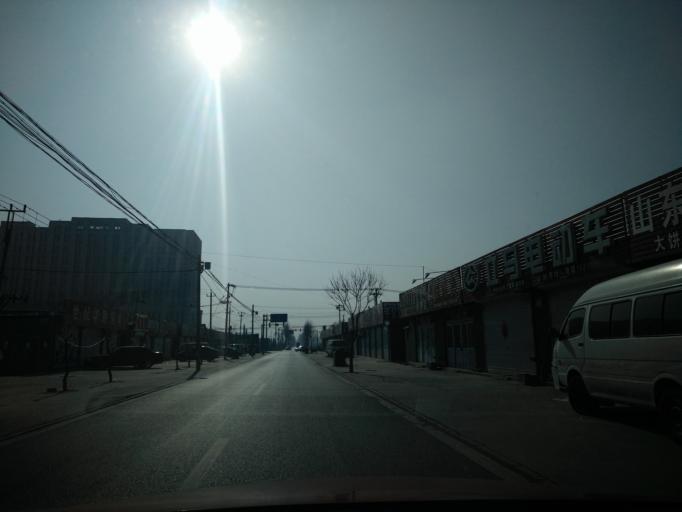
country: CN
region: Beijing
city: Yinghai
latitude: 39.7086
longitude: 116.4575
